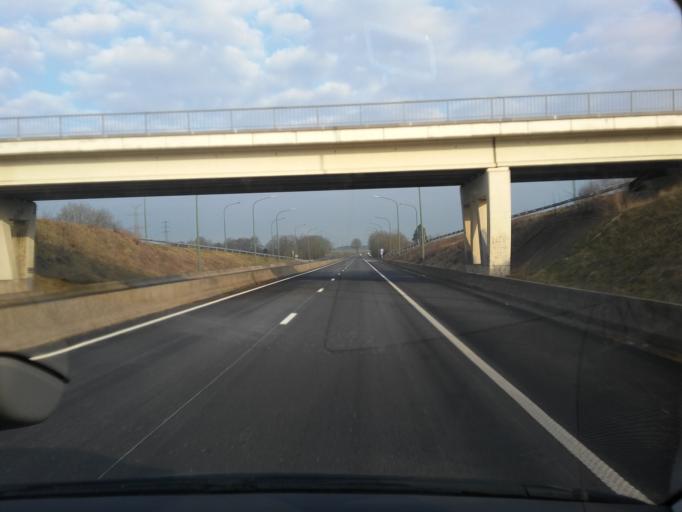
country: BE
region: Wallonia
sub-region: Province du Luxembourg
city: Martelange
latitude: 49.8637
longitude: 5.7183
